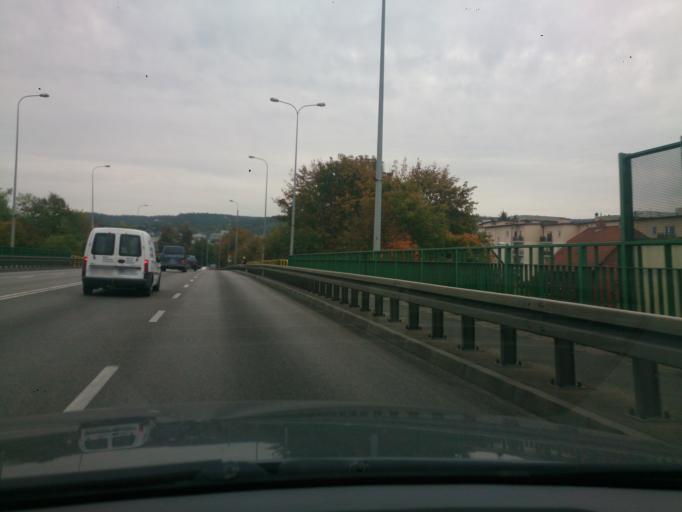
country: PL
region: Pomeranian Voivodeship
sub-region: Powiat wejherowski
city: Rumia
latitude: 54.5679
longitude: 18.3889
